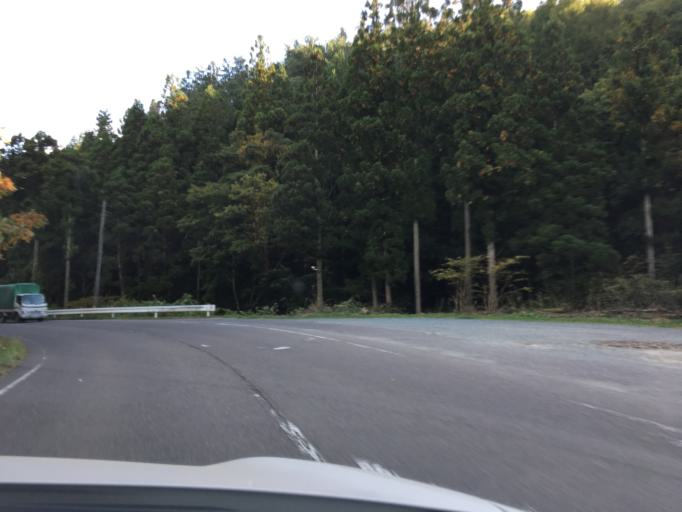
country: JP
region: Fukushima
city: Funehikimachi-funehiki
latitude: 37.3260
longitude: 140.5913
